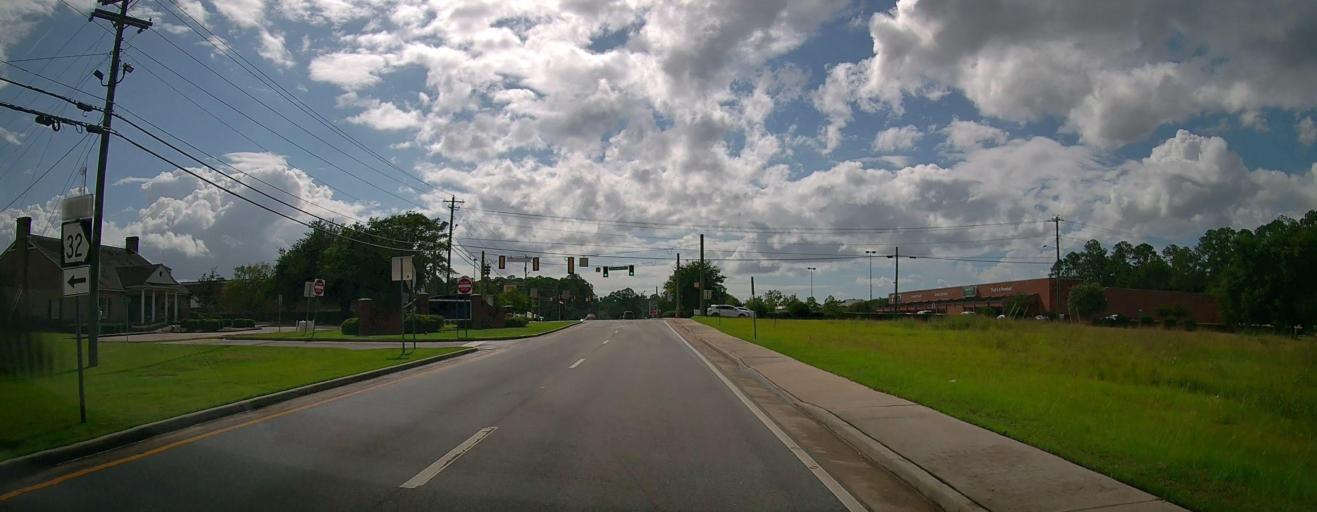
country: US
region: Georgia
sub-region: Coffee County
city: Douglas
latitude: 31.5092
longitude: -82.8591
